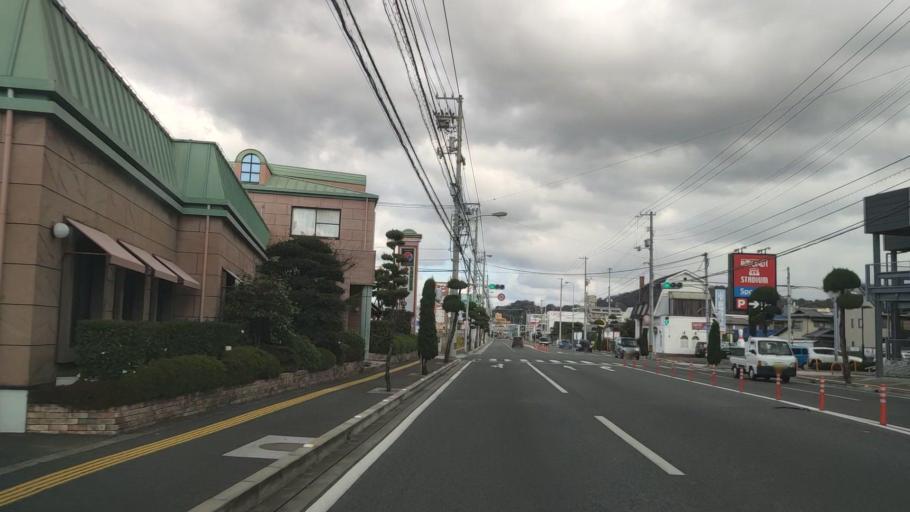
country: JP
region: Ehime
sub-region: Shikoku-chuo Shi
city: Matsuyama
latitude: 33.8665
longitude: 132.7511
